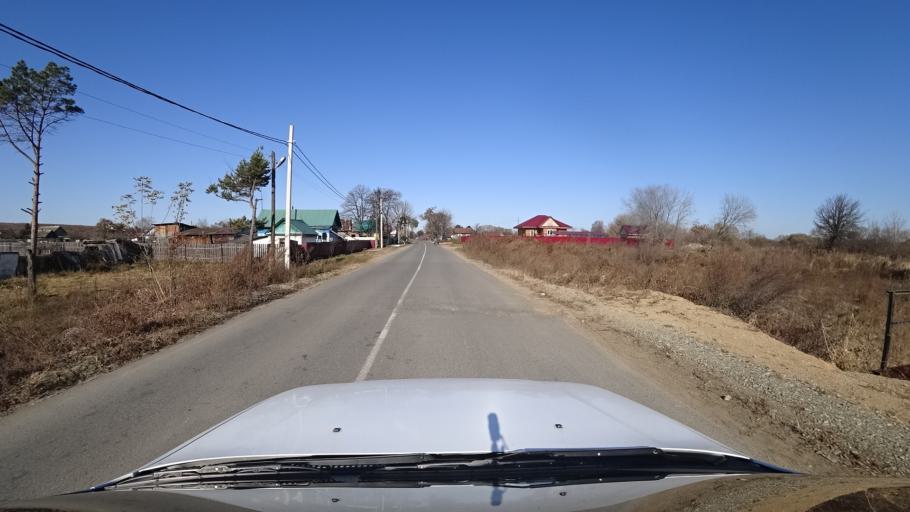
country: RU
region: Primorskiy
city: Dal'nerechensk
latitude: 45.9340
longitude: 133.7094
